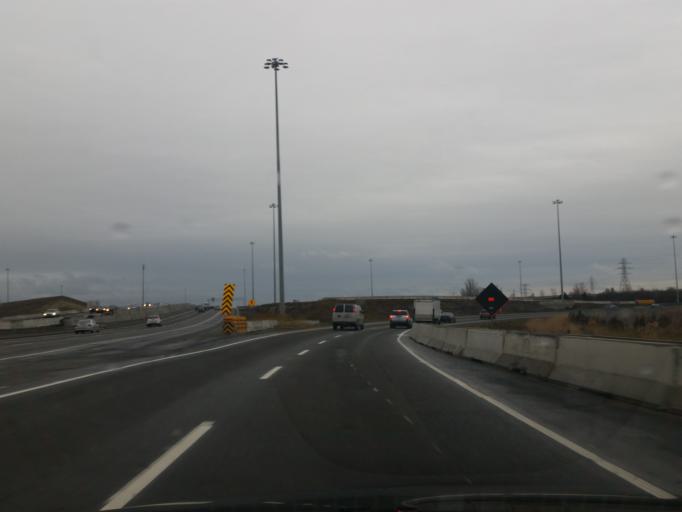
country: CA
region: Quebec
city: Quebec
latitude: 46.8350
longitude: -71.2687
